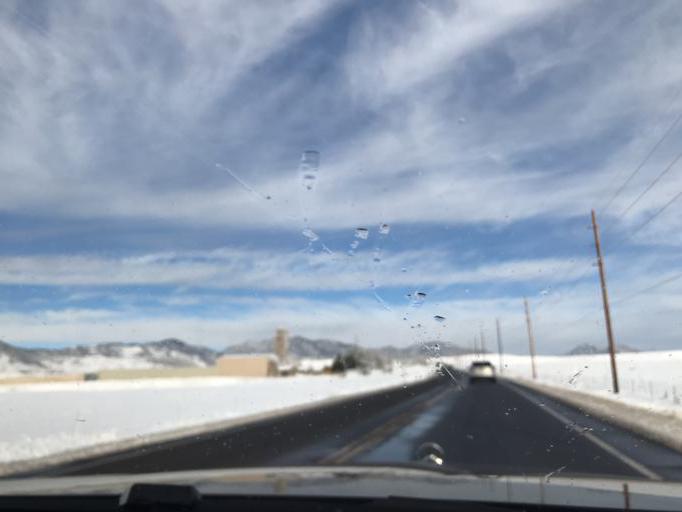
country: US
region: Colorado
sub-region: Boulder County
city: Superior
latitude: 39.8573
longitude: -105.1897
